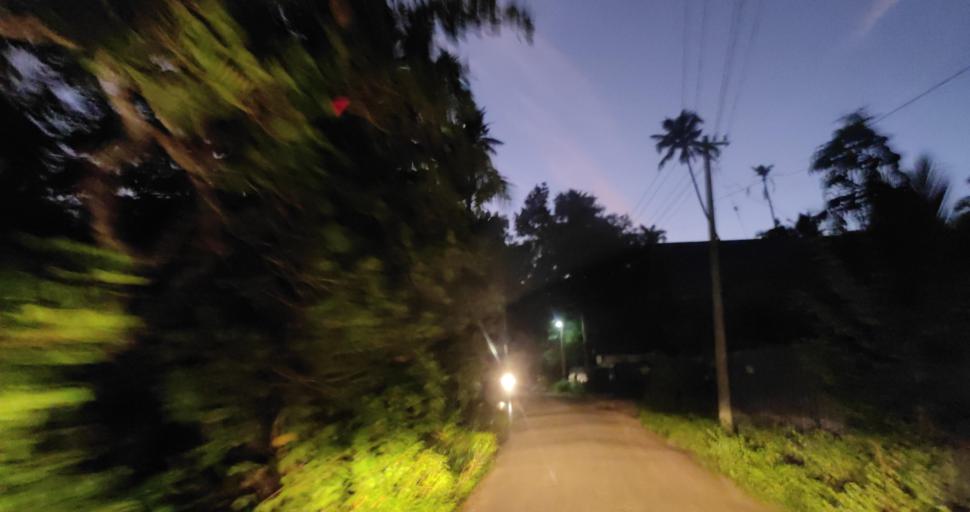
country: IN
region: Kerala
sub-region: Alappuzha
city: Shertallai
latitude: 9.6220
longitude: 76.3537
